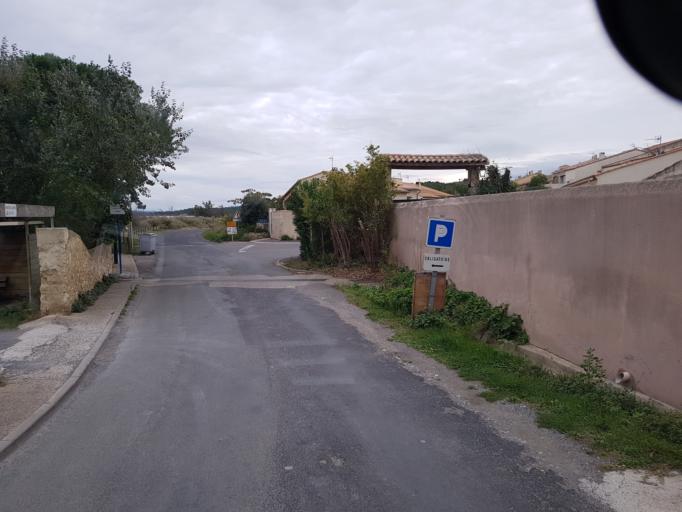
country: FR
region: Languedoc-Roussillon
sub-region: Departement de l'Aude
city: Peyriac-de-Mer
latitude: 43.1217
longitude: 2.9909
